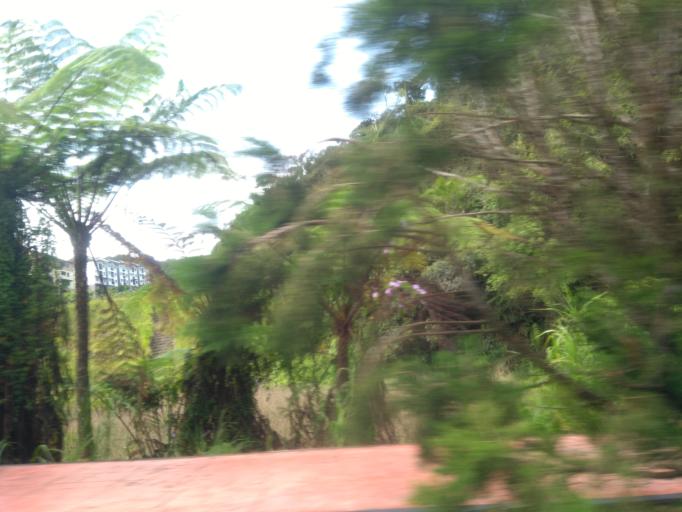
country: MY
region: Pahang
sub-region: Cameron Highlands
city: Tanah Rata
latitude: 4.4684
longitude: 101.3717
